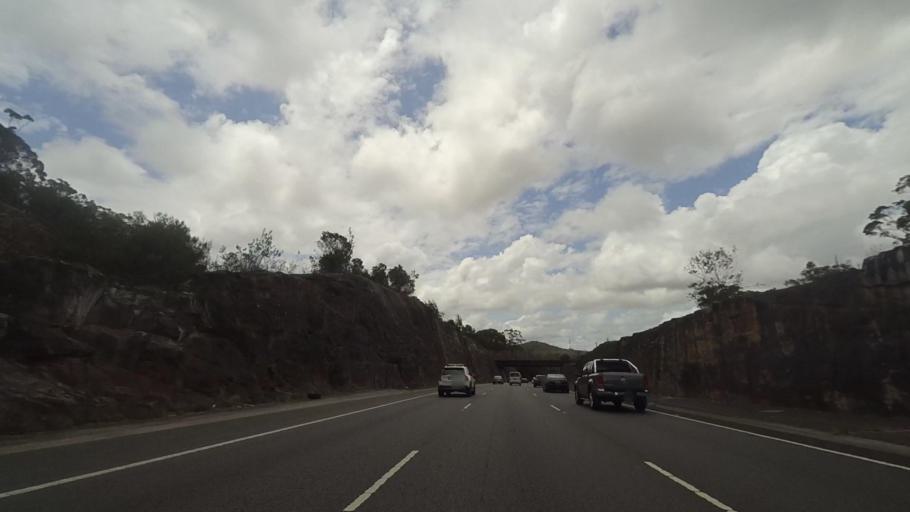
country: AU
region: New South Wales
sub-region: Gosford Shire
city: Umina
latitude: -33.4655
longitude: 151.1945
